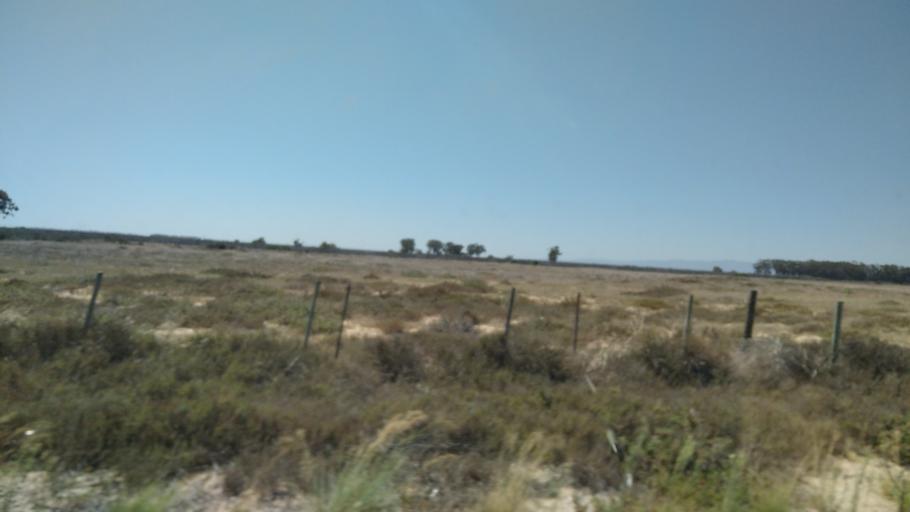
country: ZA
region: Western Cape
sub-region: West Coast District Municipality
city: Vredenburg
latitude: -32.9903
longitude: 18.1634
